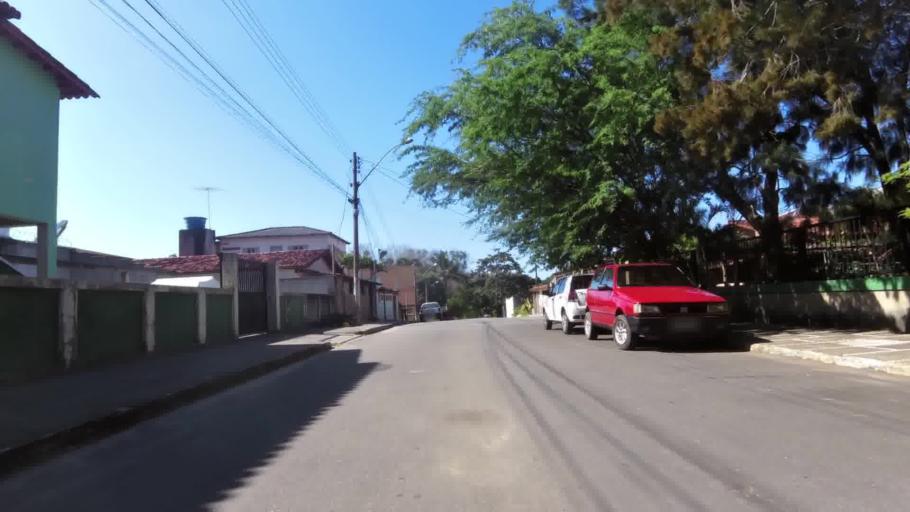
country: BR
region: Espirito Santo
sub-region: Guarapari
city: Guarapari
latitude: -20.7359
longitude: -40.5412
